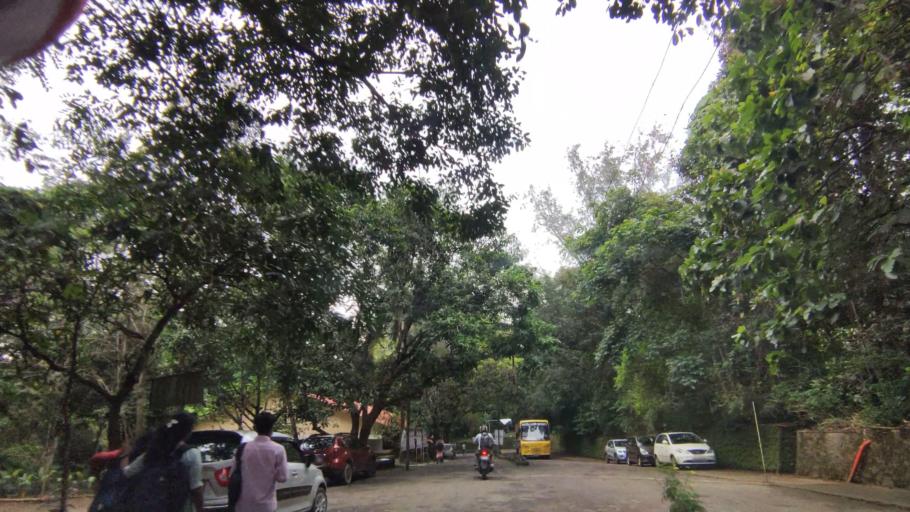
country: IN
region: Kerala
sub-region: Kottayam
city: Kottayam
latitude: 9.6587
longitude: 76.5325
